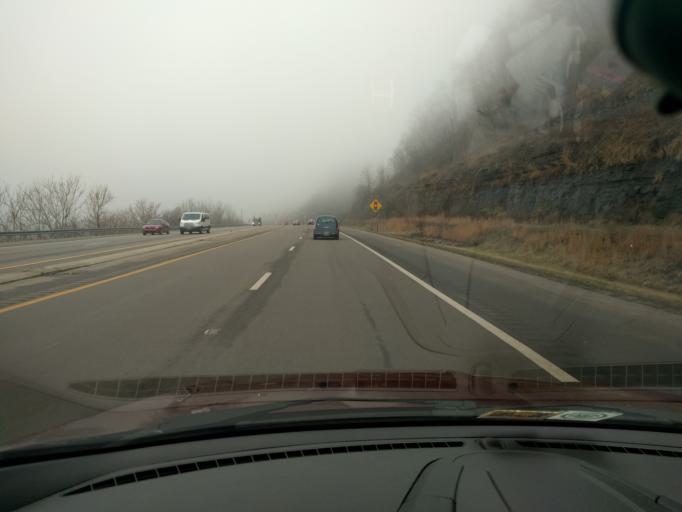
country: US
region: West Virginia
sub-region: Kanawha County
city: Chesapeake
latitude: 38.2092
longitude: -81.5075
